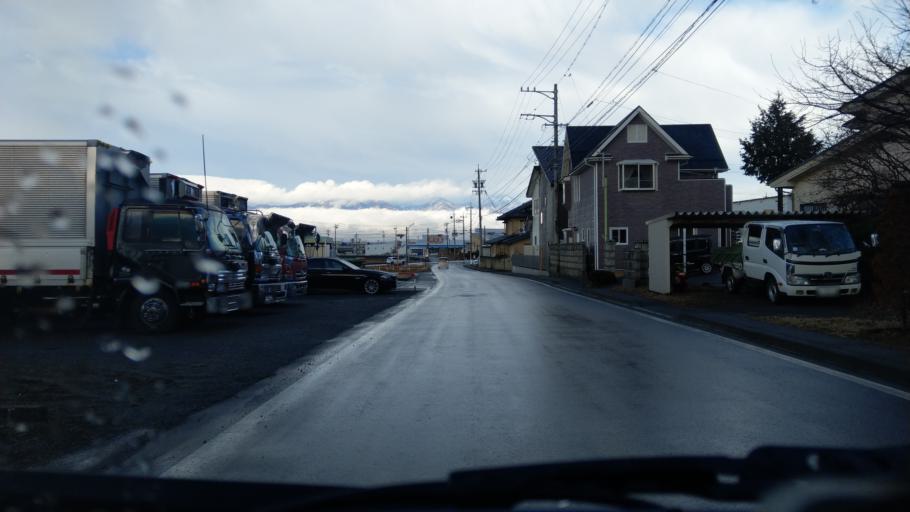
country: JP
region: Nagano
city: Kamimaruko
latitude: 36.2749
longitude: 138.3190
